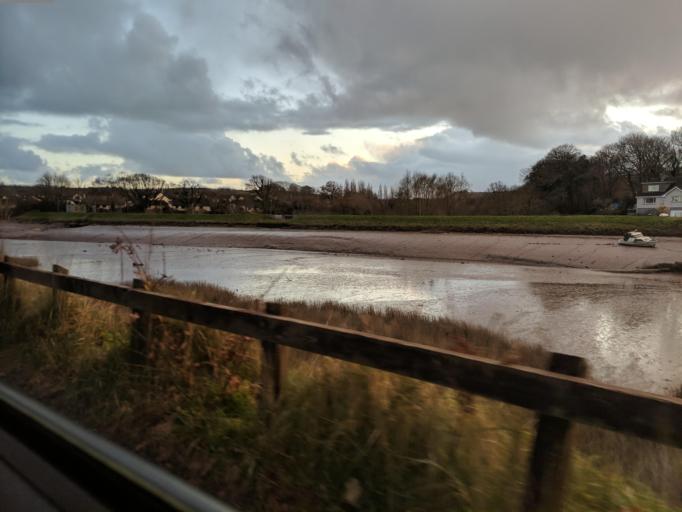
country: GB
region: England
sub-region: Devon
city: Fremington
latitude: 51.0765
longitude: -4.1197
